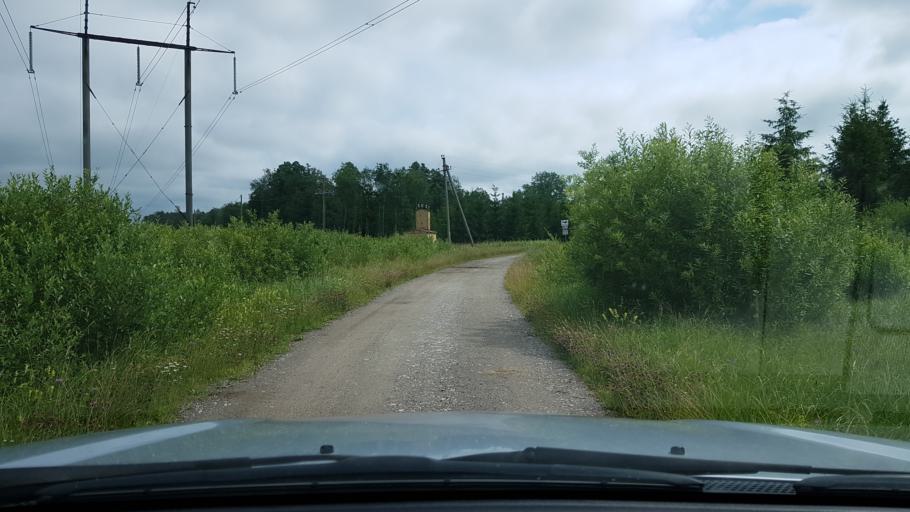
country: EE
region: Ida-Virumaa
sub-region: Narva-Joesuu linn
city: Narva-Joesuu
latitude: 59.3644
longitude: 28.0756
